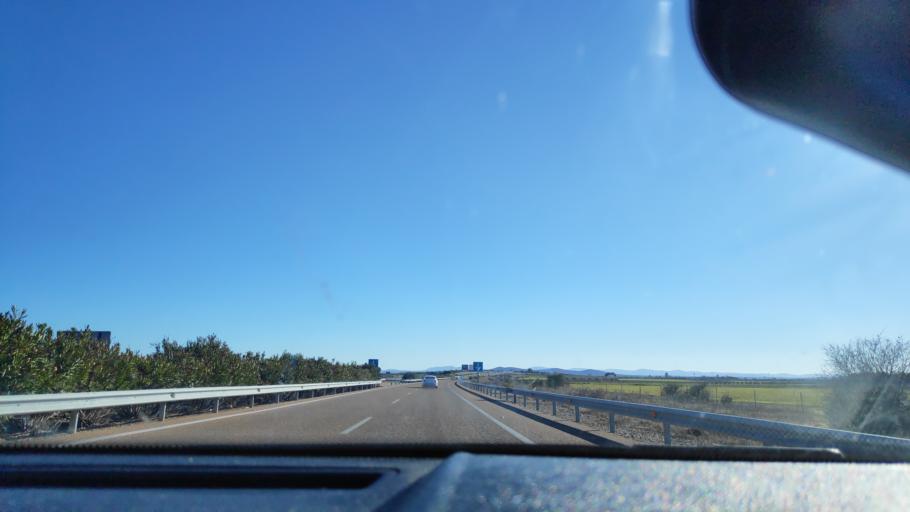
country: ES
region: Extremadura
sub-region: Provincia de Badajoz
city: Puebla de Sancho Perez
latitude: 38.4072
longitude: -6.3414
